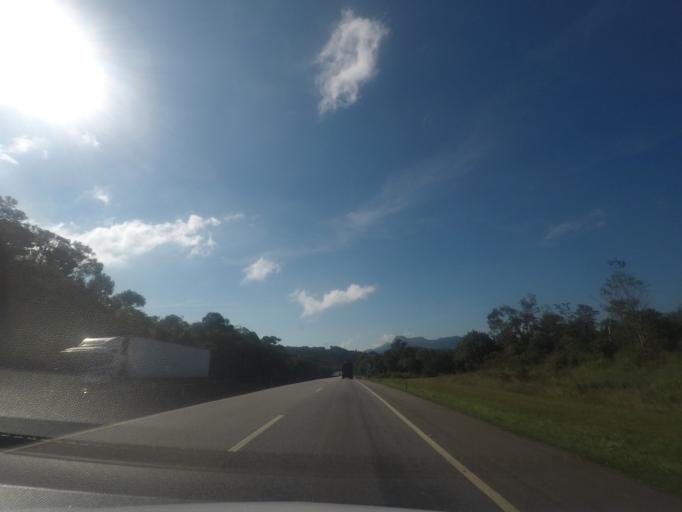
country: BR
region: Parana
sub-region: Piraquara
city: Piraquara
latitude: -25.5892
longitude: -48.9387
